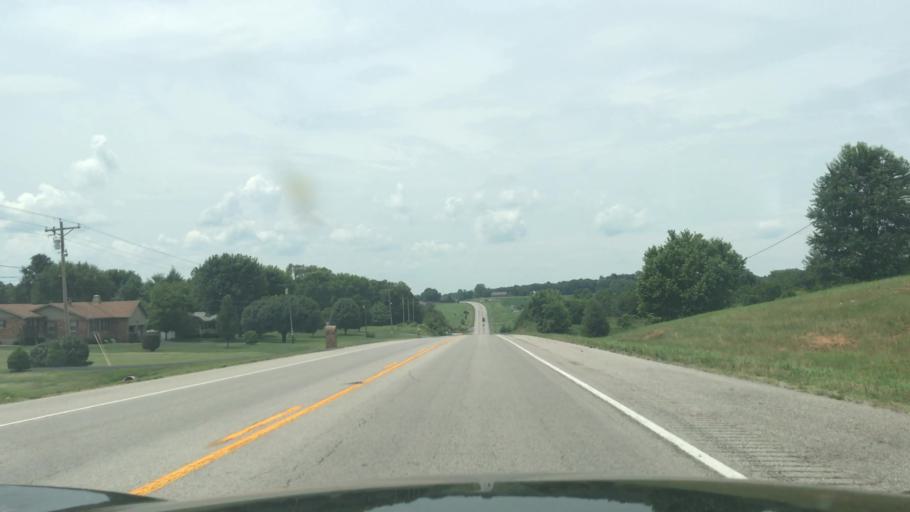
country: US
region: Kentucky
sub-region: Green County
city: Greensburg
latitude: 37.2970
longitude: -85.4594
